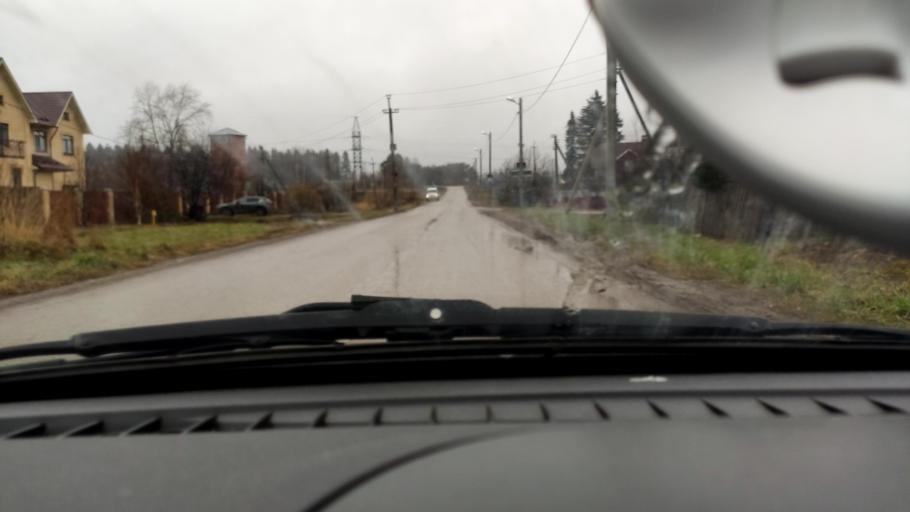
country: RU
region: Perm
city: Perm
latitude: 58.0393
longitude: 56.4082
